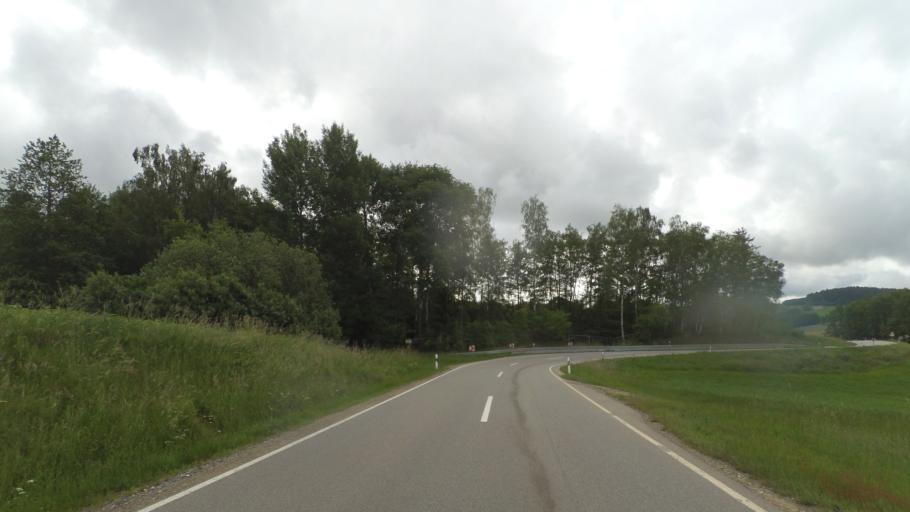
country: DE
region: Bavaria
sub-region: Lower Bavaria
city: Prackenbach
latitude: 49.0996
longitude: 12.7909
